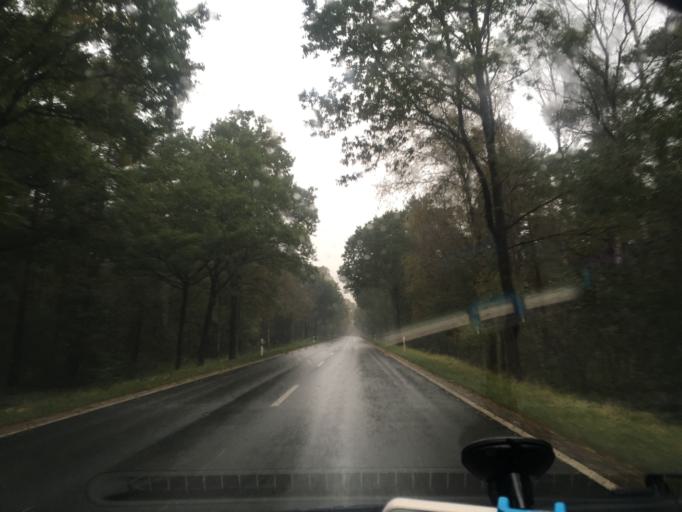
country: DE
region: Lower Saxony
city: Bispingen
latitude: 53.0523
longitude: 9.9926
